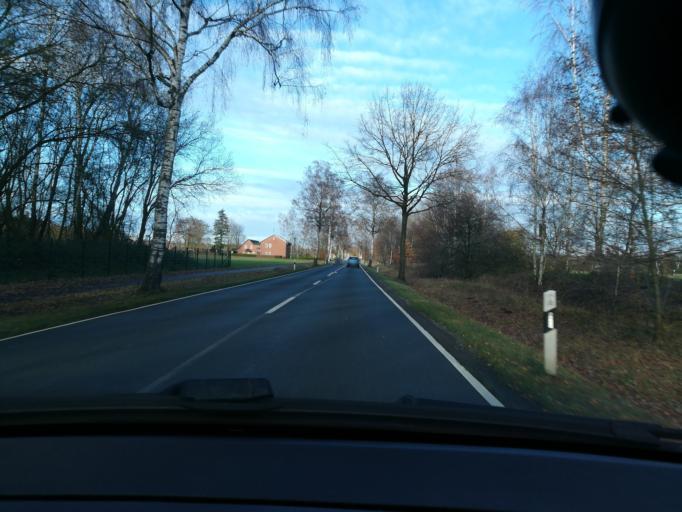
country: DE
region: Lower Saxony
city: Schwaforden
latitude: 52.7279
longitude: 8.8159
